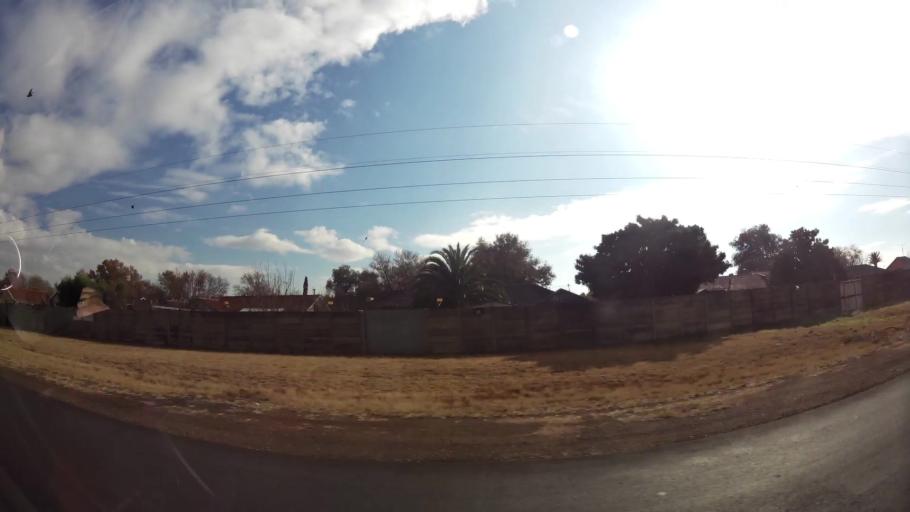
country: ZA
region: Gauteng
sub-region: Sedibeng District Municipality
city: Meyerton
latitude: -26.5571
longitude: 28.0410
